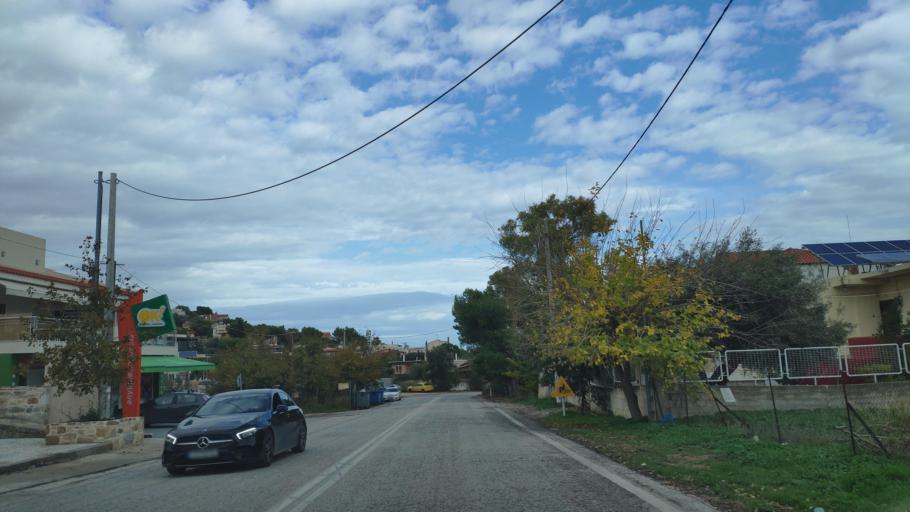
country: GR
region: Attica
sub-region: Nomarchia Anatolikis Attikis
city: Artemida
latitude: 37.9319
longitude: 24.0057
